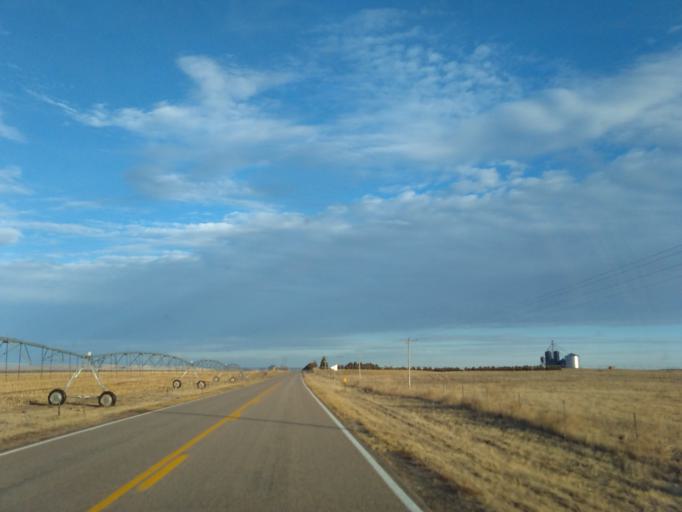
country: US
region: Nebraska
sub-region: Morrill County
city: Bridgeport
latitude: 41.5983
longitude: -102.9609
